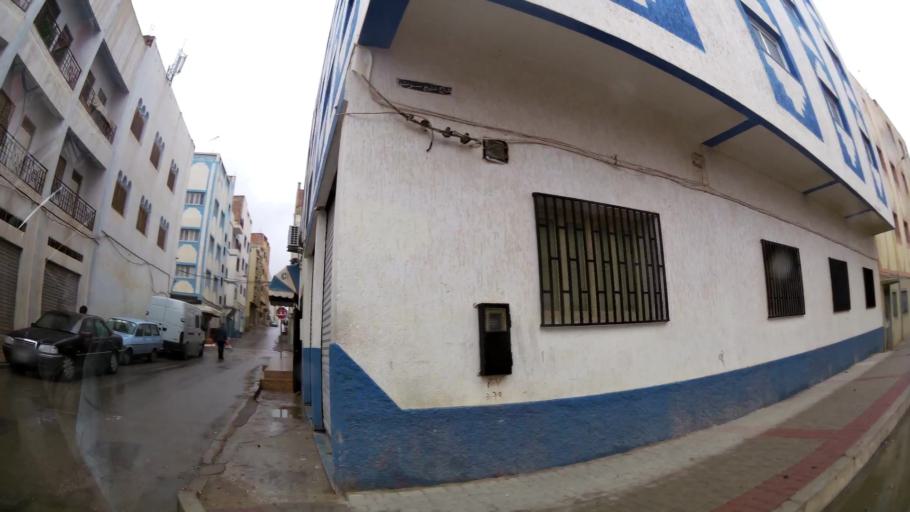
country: MA
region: Taza-Al Hoceima-Taounate
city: Imzourene
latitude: 35.1414
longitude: -3.8510
